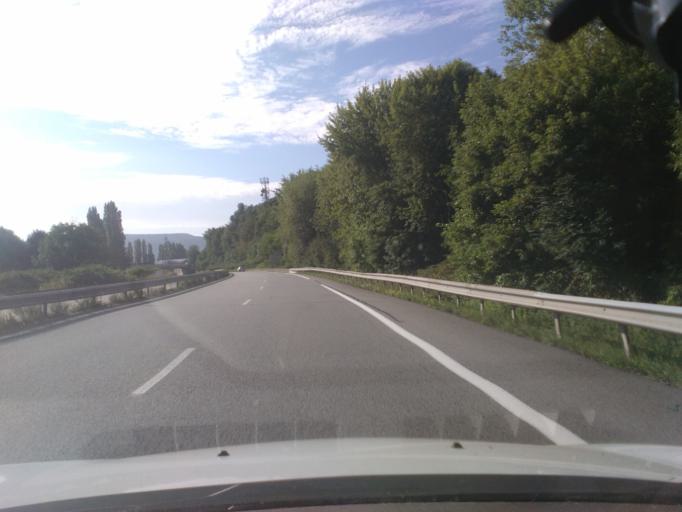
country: FR
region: Lorraine
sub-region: Departement des Vosges
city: Remiremont
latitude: 48.0204
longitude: 6.5951
